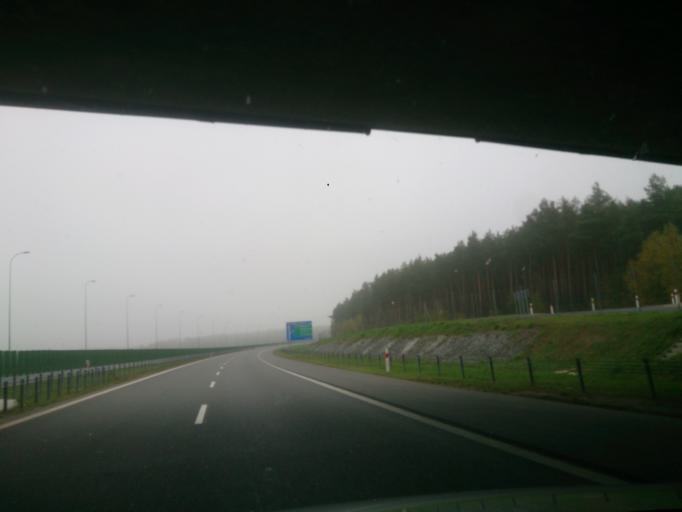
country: PL
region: Kujawsko-Pomorskie
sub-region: Powiat swiecki
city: Warlubie
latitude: 53.4653
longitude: 18.6201
